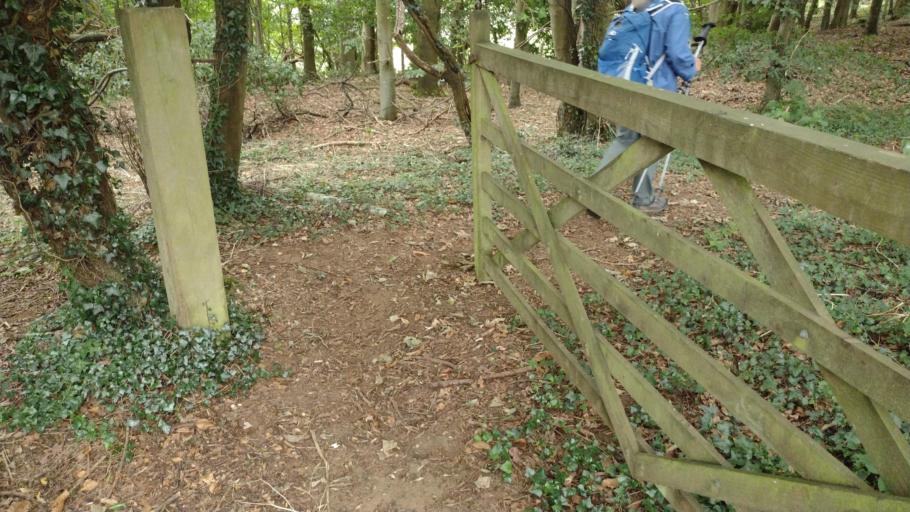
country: GB
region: England
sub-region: Oxfordshire
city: Hook Norton
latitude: 52.0638
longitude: -1.4998
